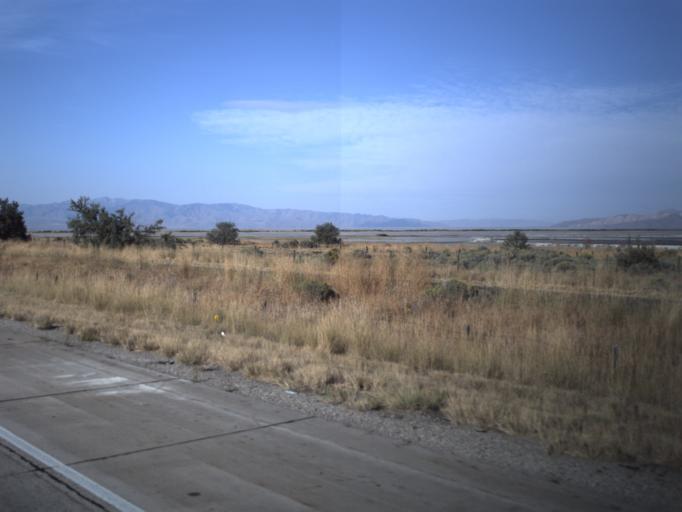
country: US
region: Utah
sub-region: Salt Lake County
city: Magna
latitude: 40.7654
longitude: -112.1586
